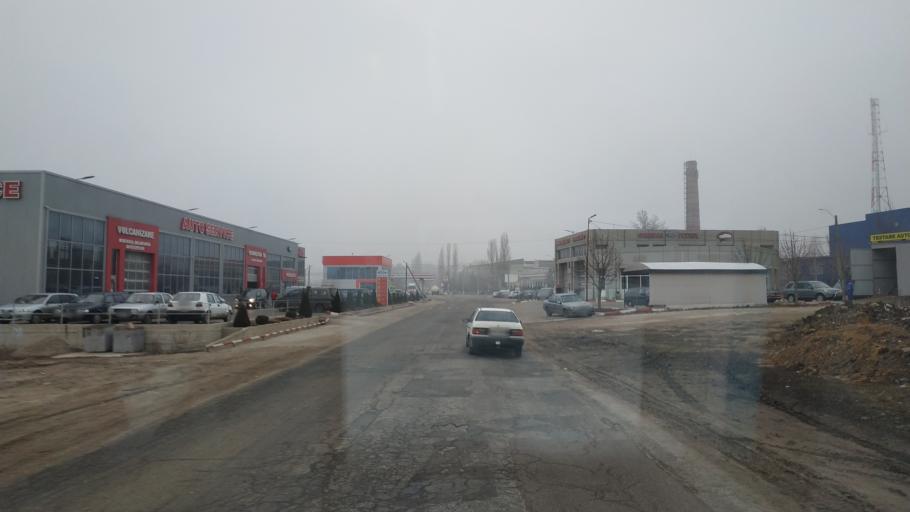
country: MD
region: Laloveni
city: Ialoveni
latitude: 46.9494
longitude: 28.7677
